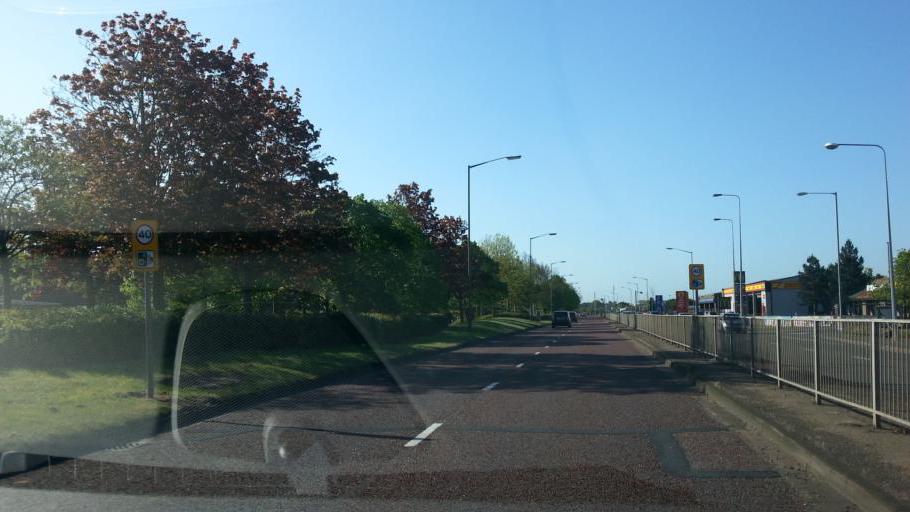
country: GB
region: England
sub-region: Peterborough
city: Peterborough
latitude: 52.5821
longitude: -0.2520
